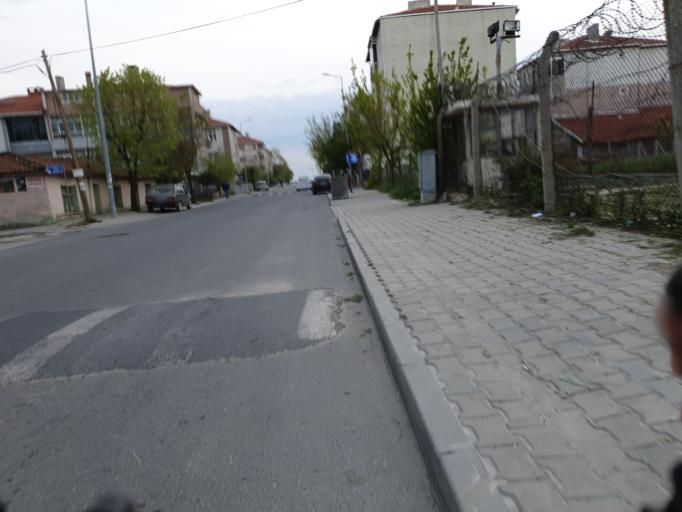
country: TR
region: Tekirdag
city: Saray
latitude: 41.4361
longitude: 27.9149
